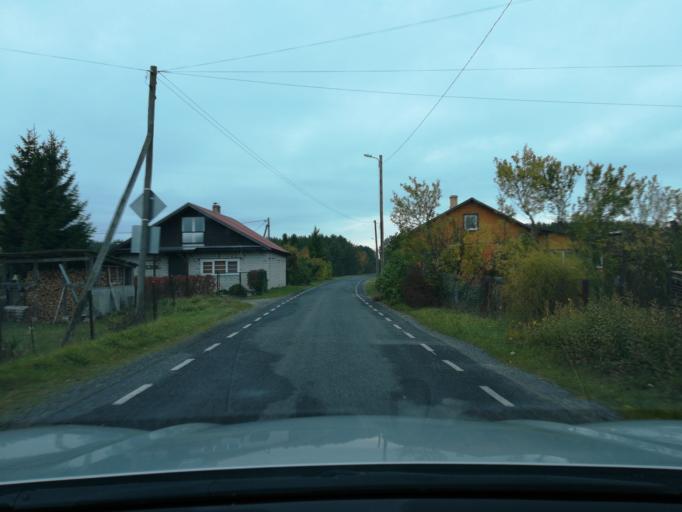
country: EE
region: Ida-Virumaa
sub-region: Johvi vald
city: Johvi
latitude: 59.0109
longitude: 27.4260
